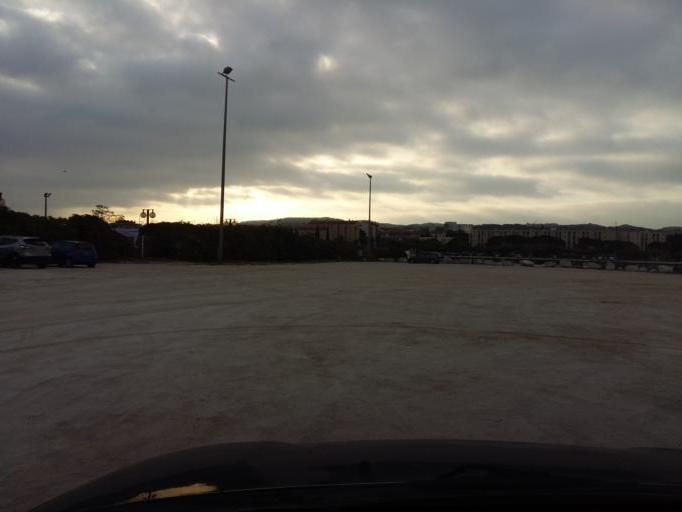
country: FR
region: Provence-Alpes-Cote d'Azur
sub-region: Departement des Bouches-du-Rhone
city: Martigues
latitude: 43.4044
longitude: 5.0451
